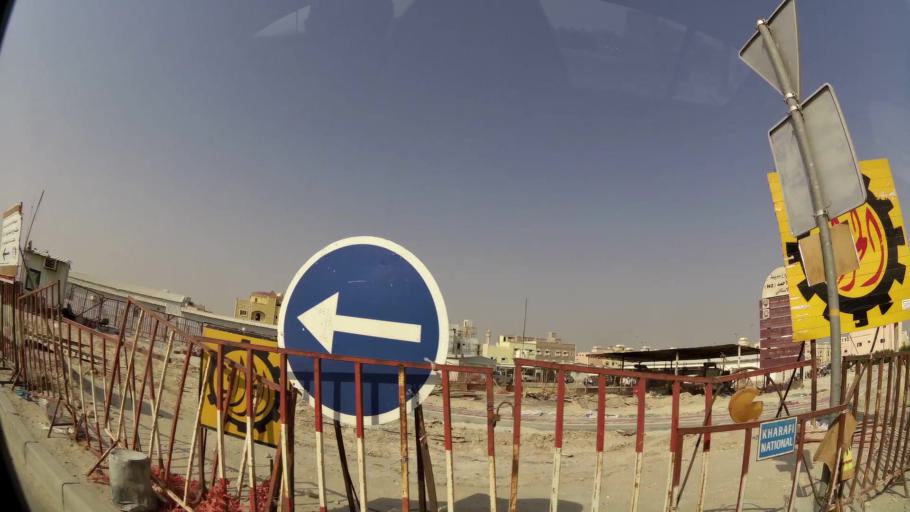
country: KW
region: Muhafazat al Jahra'
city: Al Jahra'
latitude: 29.3463
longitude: 47.7596
